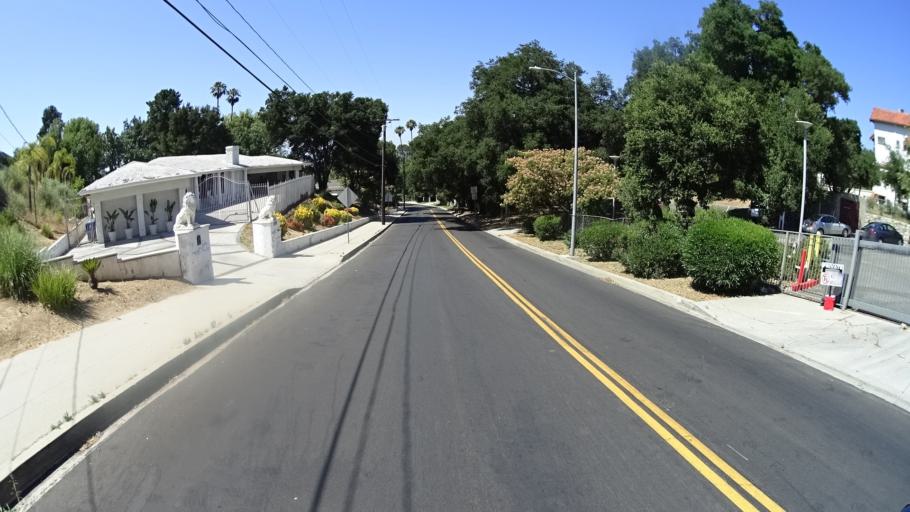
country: US
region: California
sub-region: Los Angeles County
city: Sherman Oaks
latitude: 34.1487
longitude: -118.4920
